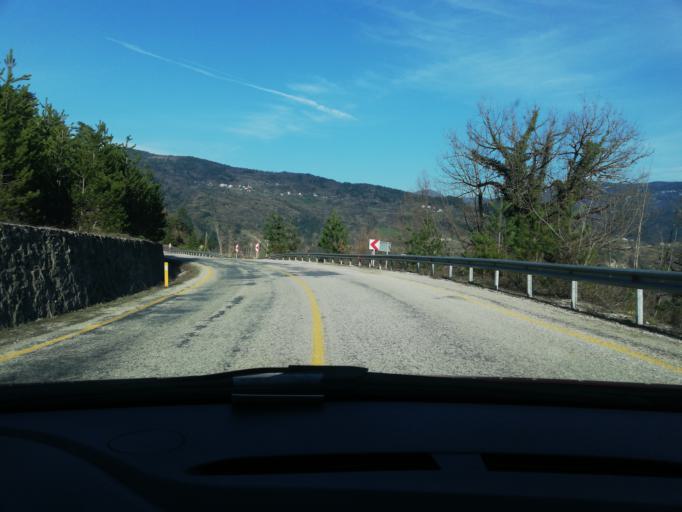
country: TR
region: Kastamonu
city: Senpazar
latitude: 41.7831
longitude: 33.1685
